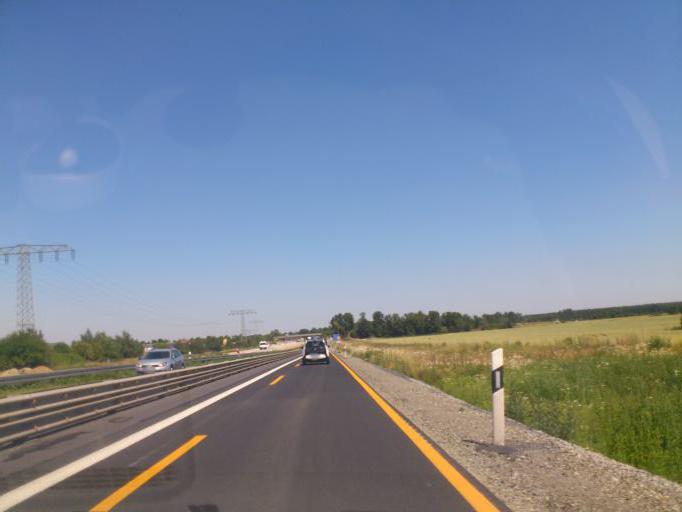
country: DE
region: Saxony
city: Radeburg
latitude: 51.2029
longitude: 13.7388
